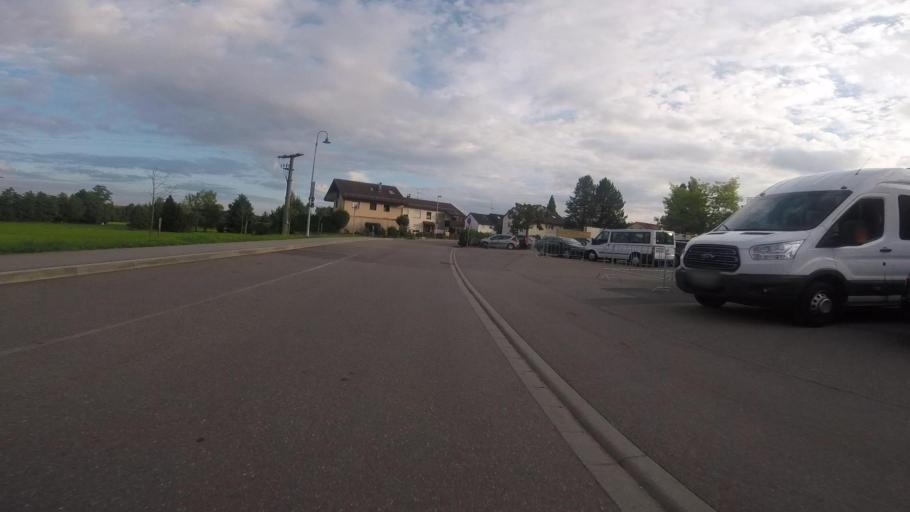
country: DE
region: Baden-Wuerttemberg
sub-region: Regierungsbezirk Stuttgart
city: Aspach
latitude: 48.9944
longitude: 9.3591
